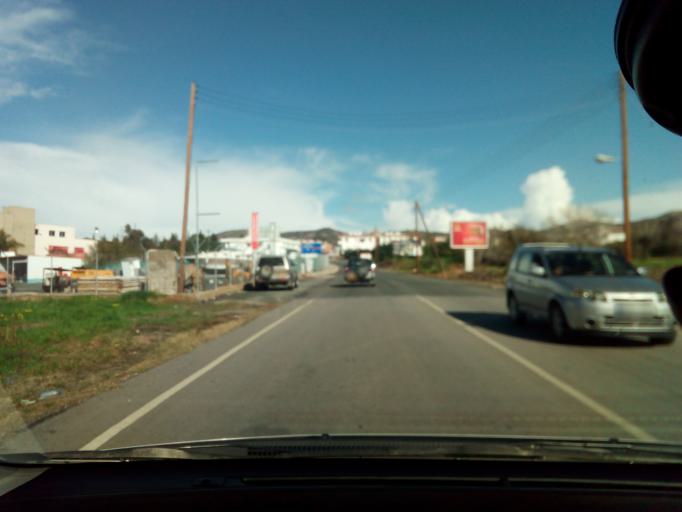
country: CY
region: Pafos
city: Mesogi
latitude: 34.8093
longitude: 32.4503
